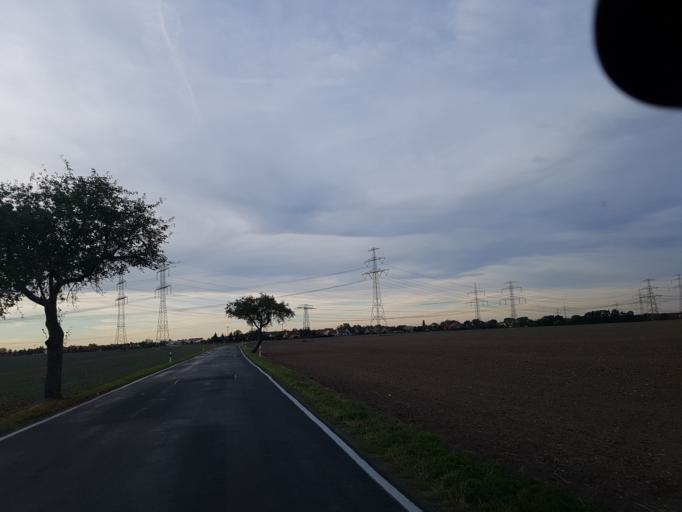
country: DE
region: Saxony
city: Wulknitz
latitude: 51.3629
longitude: 13.4055
